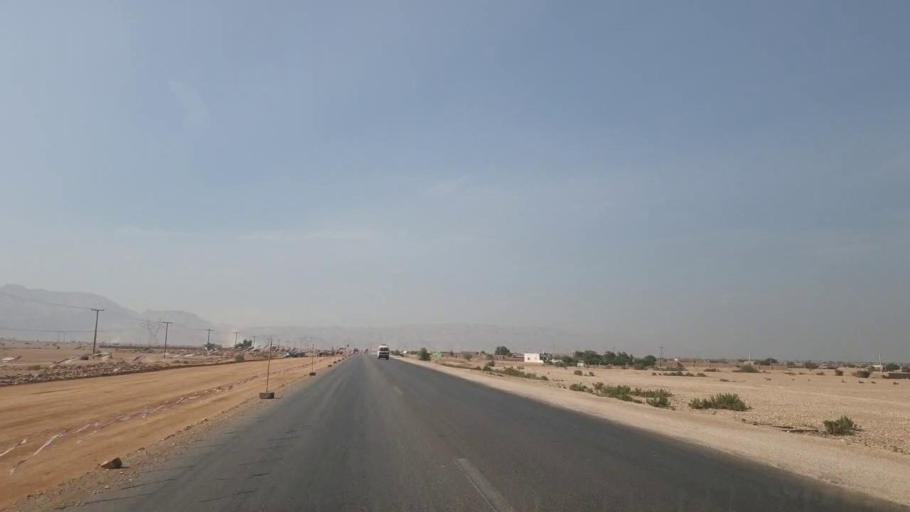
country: PK
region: Sindh
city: Sehwan
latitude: 26.1999
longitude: 67.9394
